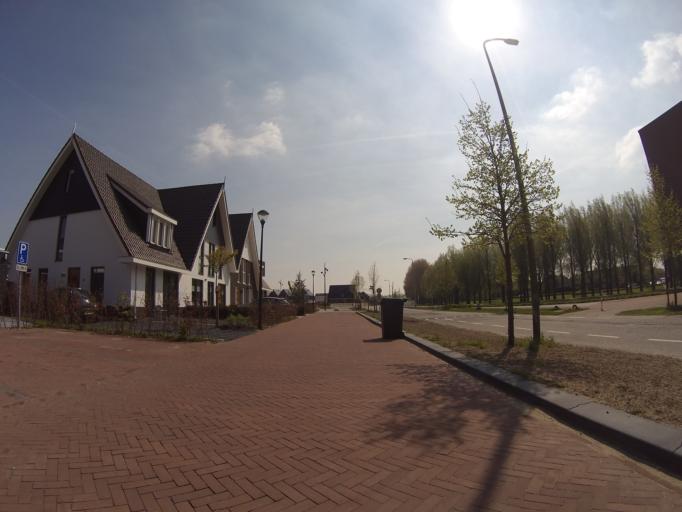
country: NL
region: North Holland
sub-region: Gemeente Huizen
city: Huizen
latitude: 52.2909
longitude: 5.2722
